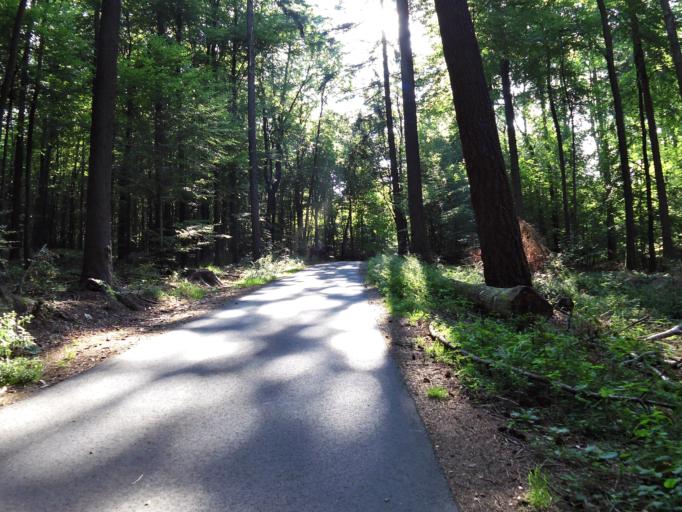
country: DE
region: Hesse
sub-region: Regierungsbezirk Darmstadt
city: Heppenheim an der Bergstrasse
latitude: 49.6716
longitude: 8.6981
